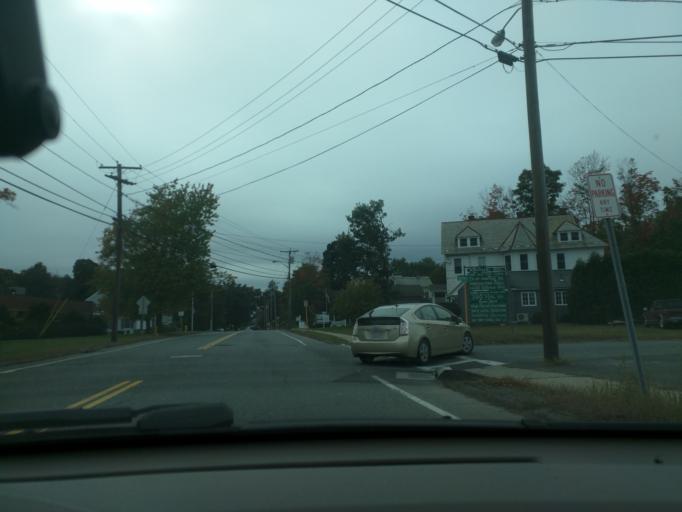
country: US
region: Massachusetts
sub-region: Hampden County
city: East Longmeadow
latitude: 42.0632
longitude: -72.5171
